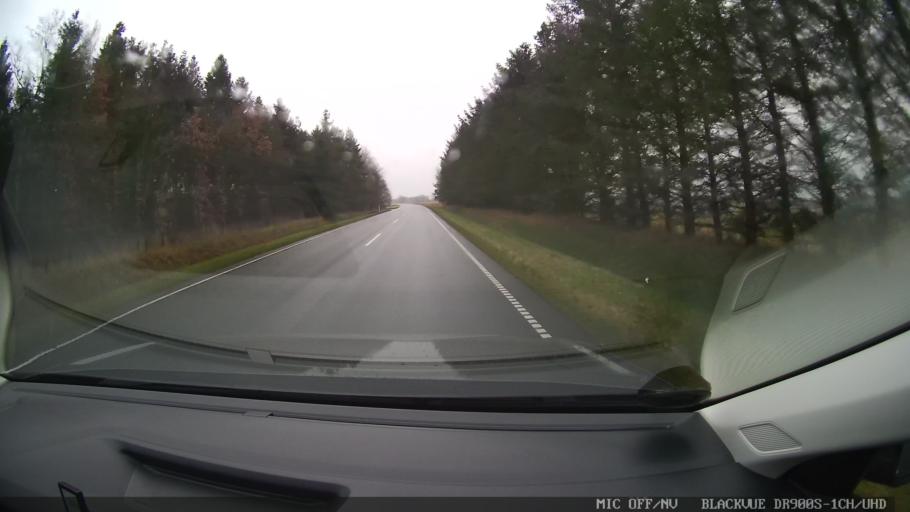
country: DK
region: Central Jutland
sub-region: Herning Kommune
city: Sunds
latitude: 56.2802
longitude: 8.9490
